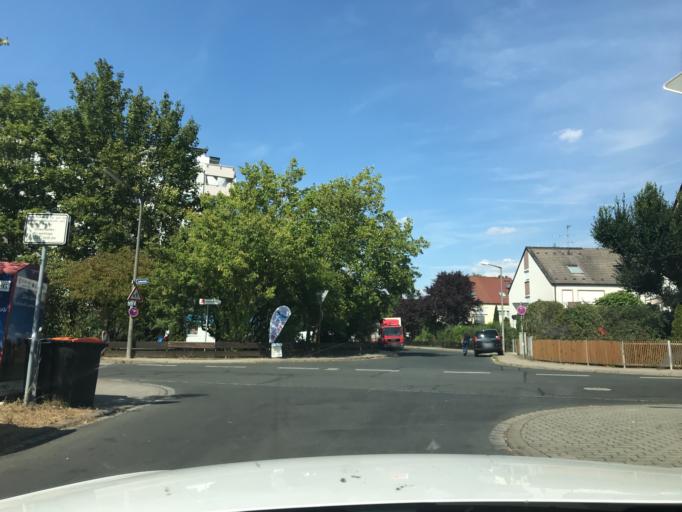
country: DE
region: Bavaria
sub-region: Regierungsbezirk Mittelfranken
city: Erlangen
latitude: 49.5522
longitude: 11.0234
